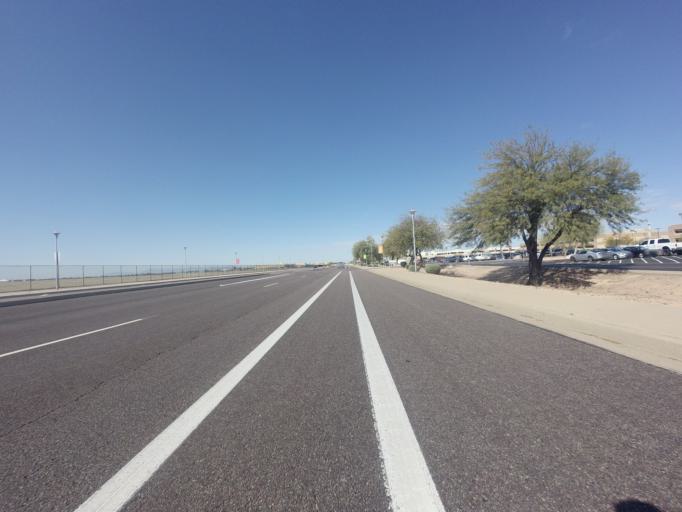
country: US
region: Arizona
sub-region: Maricopa County
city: Mesa
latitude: 33.4665
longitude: -111.7213
